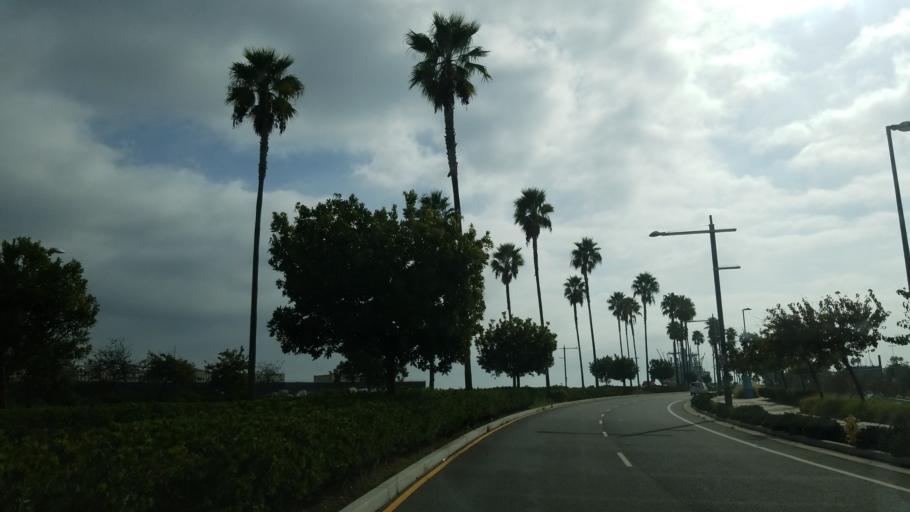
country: US
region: California
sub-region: Los Angeles County
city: San Pedro
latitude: 33.7212
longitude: -118.2754
